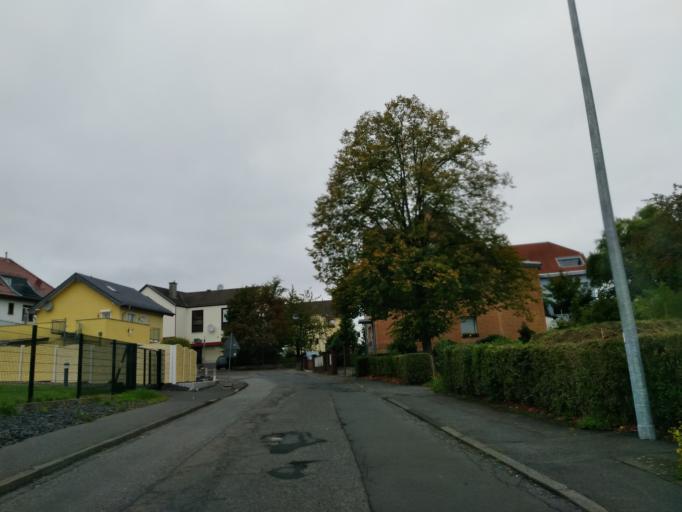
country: DE
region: Rheinland-Pfalz
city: Windhagen
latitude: 50.6616
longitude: 7.3032
